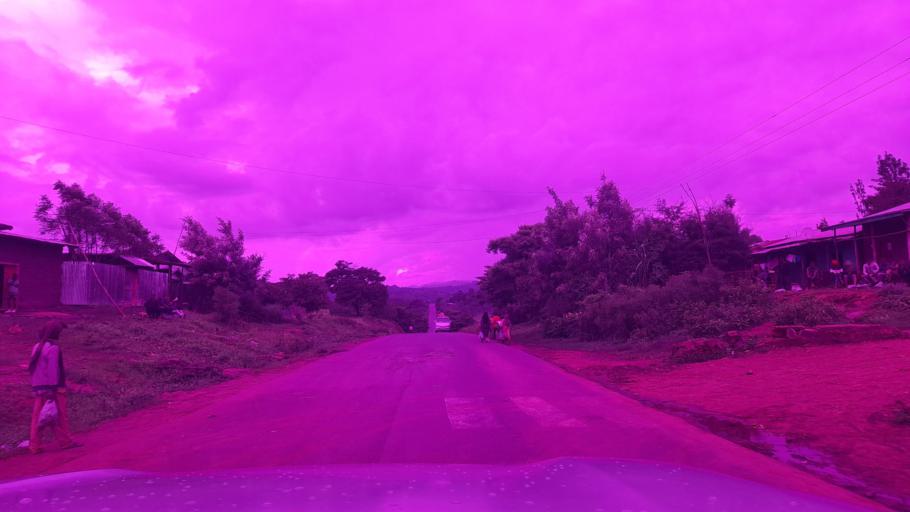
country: ET
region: Oromiya
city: Jima
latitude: 7.7590
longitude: 37.3346
